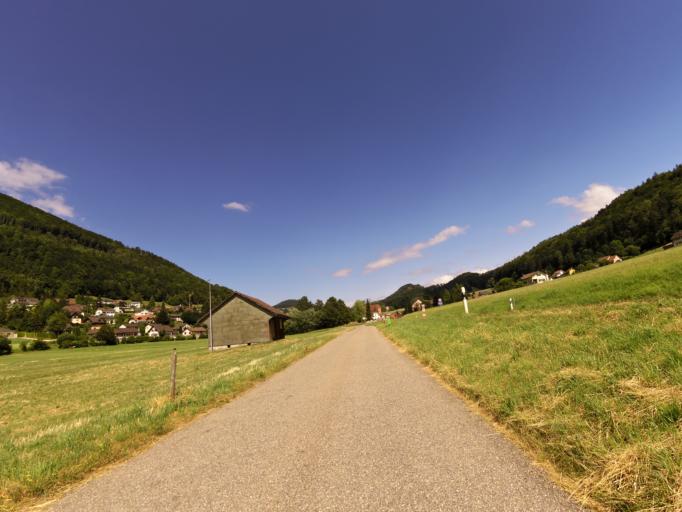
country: CH
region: Basel-Landschaft
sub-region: Bezirk Waldenburg
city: Langenbruck
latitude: 47.3317
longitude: 7.7469
